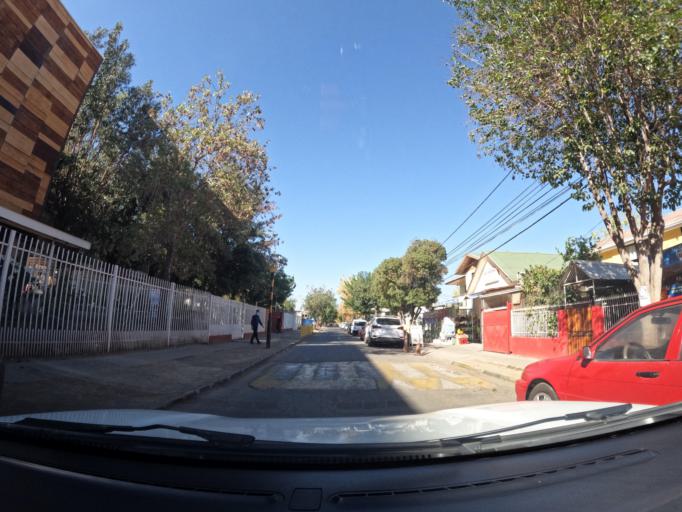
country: CL
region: Santiago Metropolitan
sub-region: Provincia de Santiago
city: Villa Presidente Frei, Nunoa, Santiago, Chile
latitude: -33.5032
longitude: -70.5785
